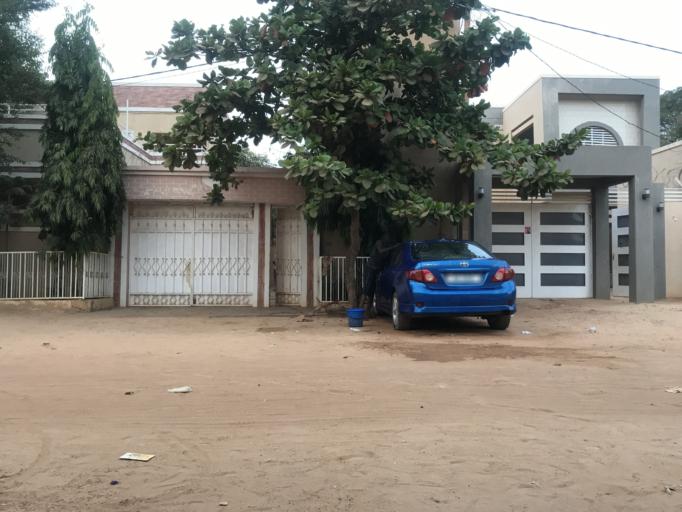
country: NE
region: Niamey
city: Niamey
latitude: 13.5480
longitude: 2.0858
